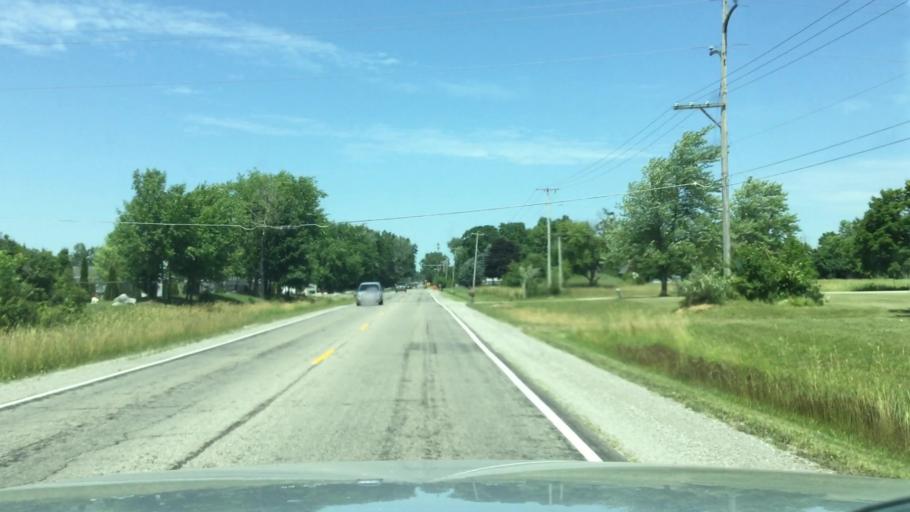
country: US
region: Michigan
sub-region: Genesee County
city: Swartz Creek
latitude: 42.9533
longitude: -83.8110
